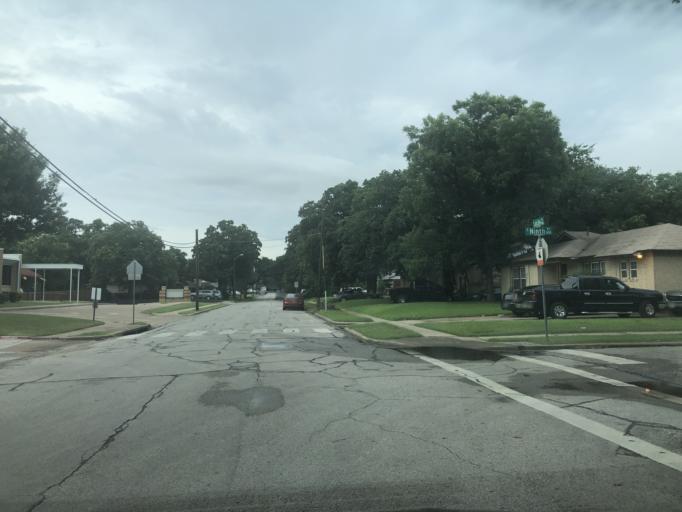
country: US
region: Texas
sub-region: Dallas County
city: Irving
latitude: 32.8058
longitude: -96.9403
